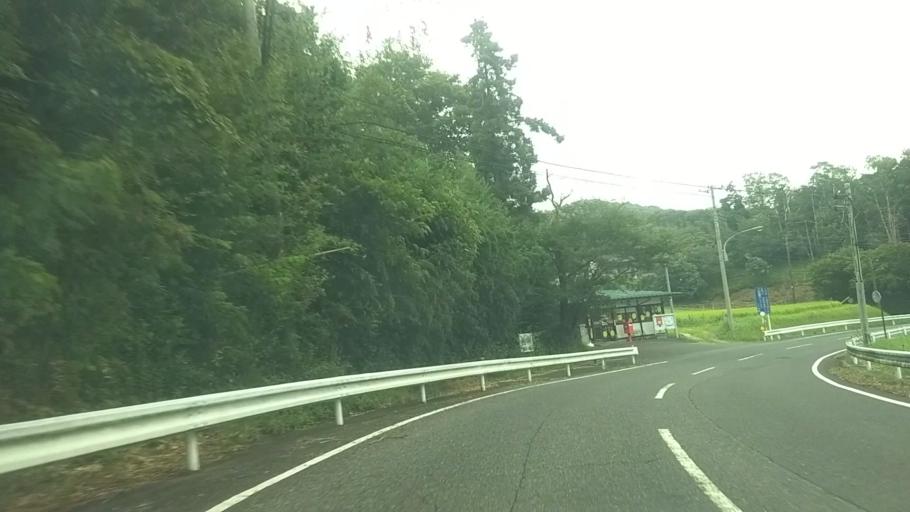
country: JP
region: Chiba
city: Kawaguchi
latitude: 35.2245
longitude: 140.0182
